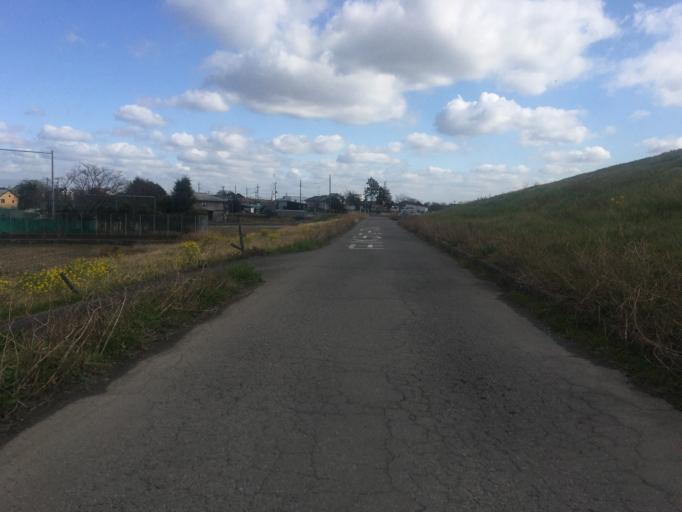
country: JP
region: Saitama
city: Shiki
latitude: 35.8660
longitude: 139.5919
